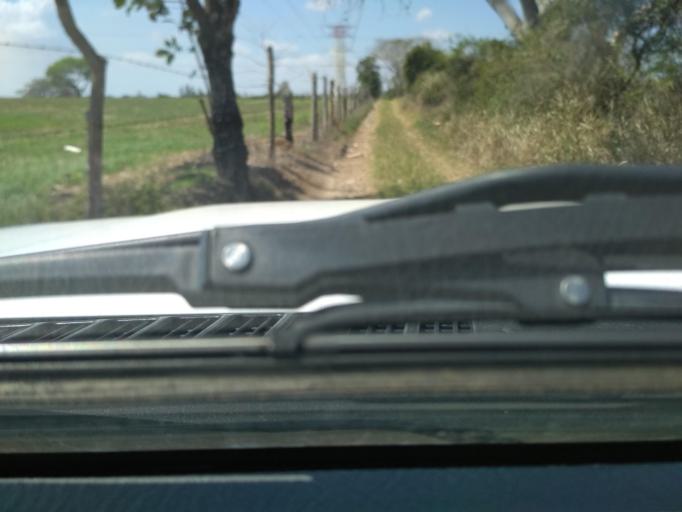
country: MX
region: Veracruz
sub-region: Veracruz
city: Las Amapolas
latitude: 19.1375
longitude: -96.2237
